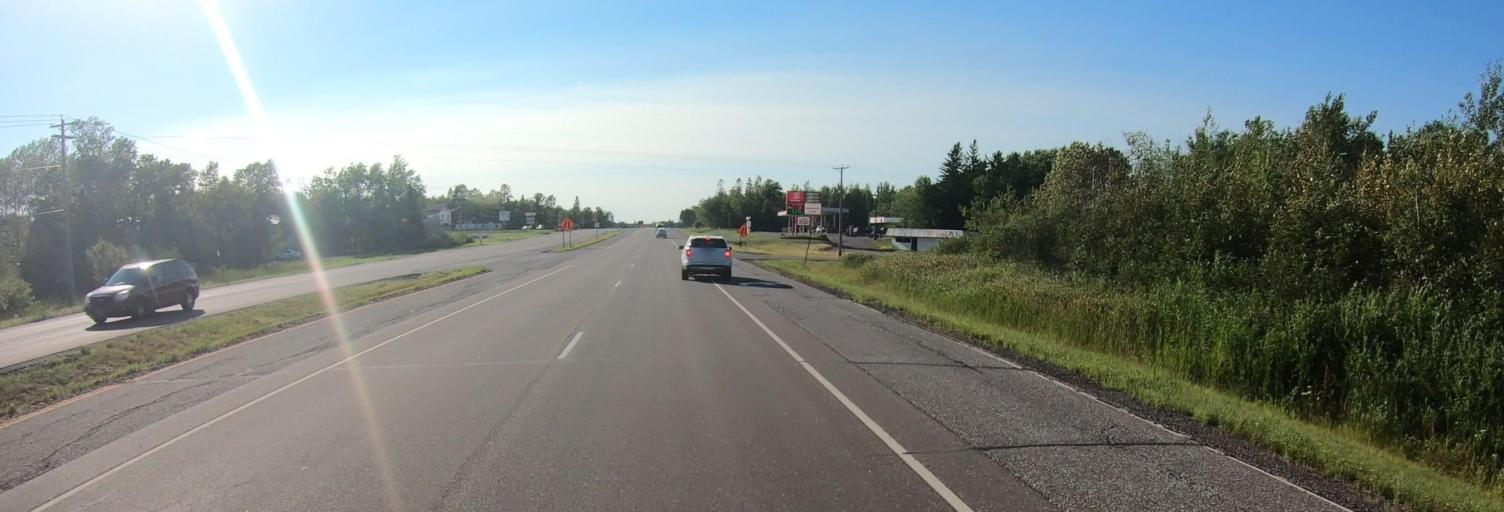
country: US
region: Minnesota
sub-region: Saint Louis County
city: Hermantown
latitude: 46.8473
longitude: -92.2692
